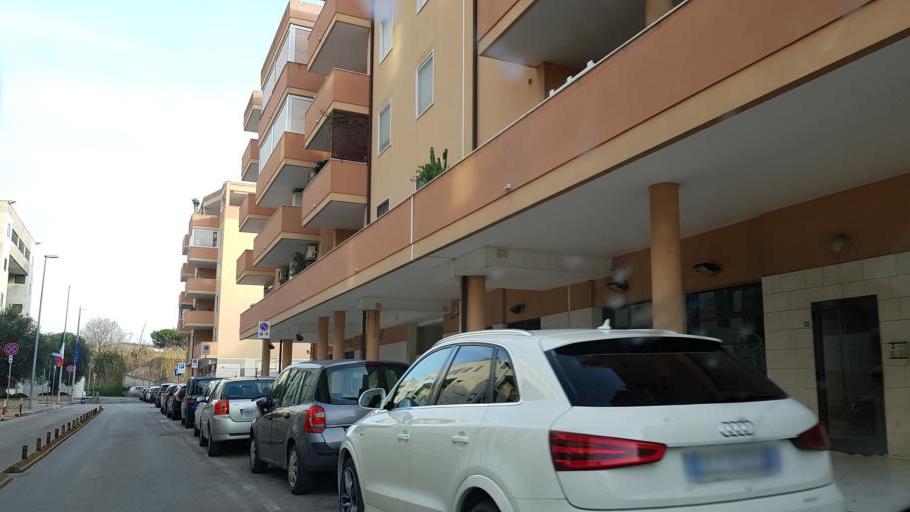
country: IT
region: Apulia
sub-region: Provincia di Brindisi
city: Brindisi
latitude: 40.6305
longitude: 17.9466
